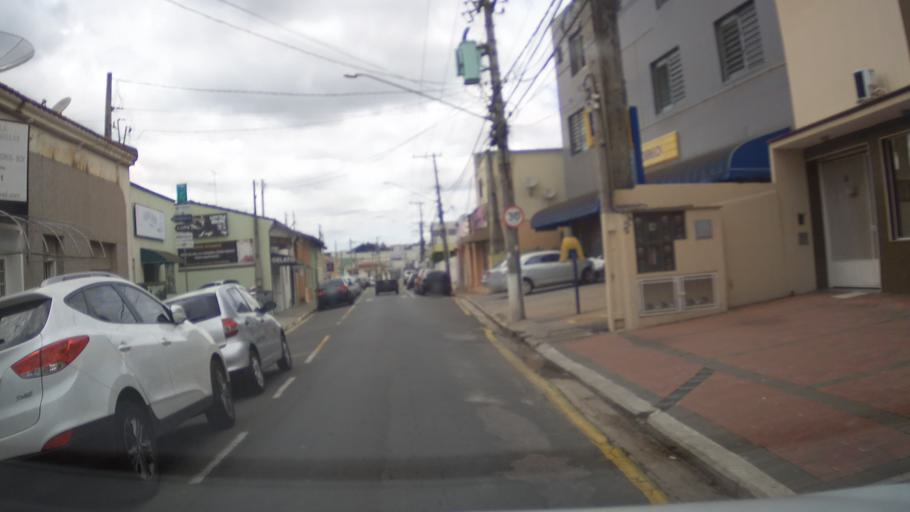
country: BR
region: Sao Paulo
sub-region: Vinhedo
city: Vinhedo
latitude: -23.0281
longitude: -46.9790
